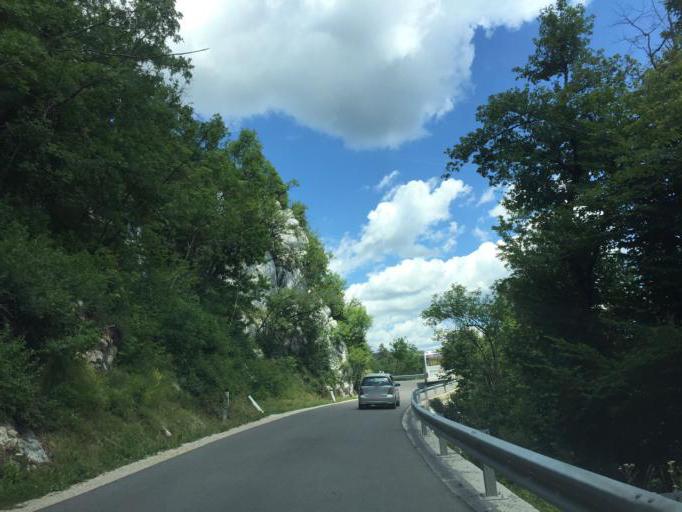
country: SI
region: Postojna
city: Postojna
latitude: 45.8181
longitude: 14.1359
